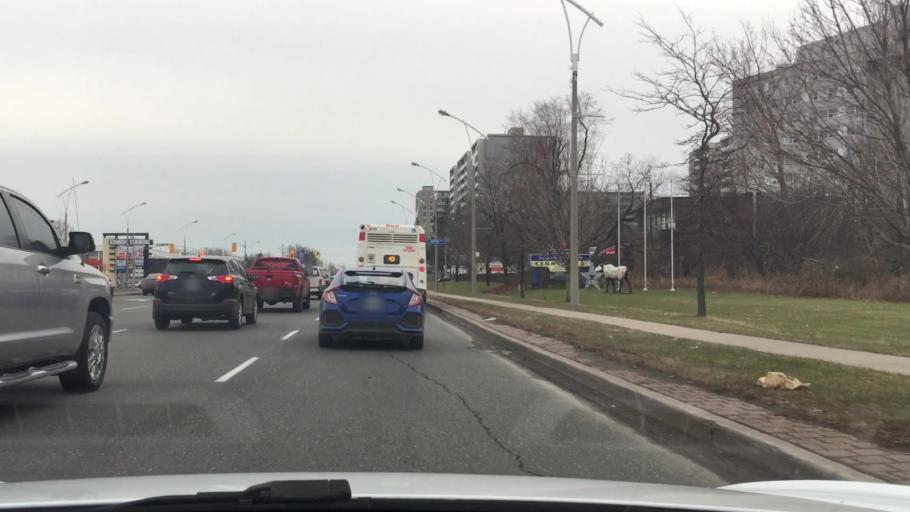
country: CA
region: Ontario
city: Scarborough
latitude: 43.7729
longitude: -79.2839
